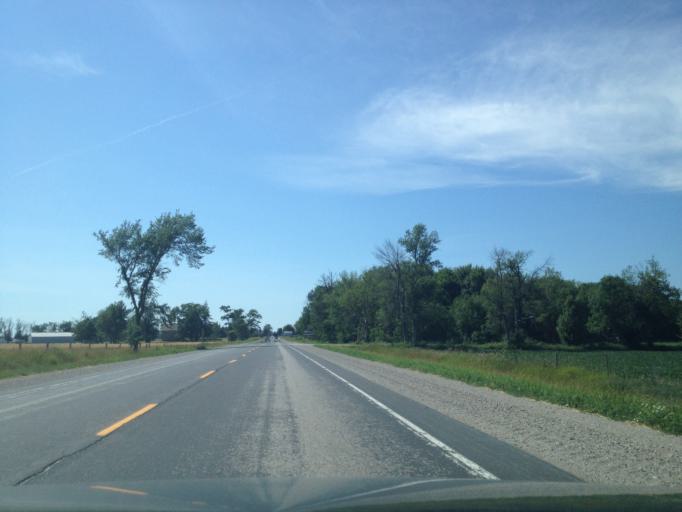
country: CA
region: Ontario
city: Stratford
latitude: 43.4975
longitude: -80.8676
